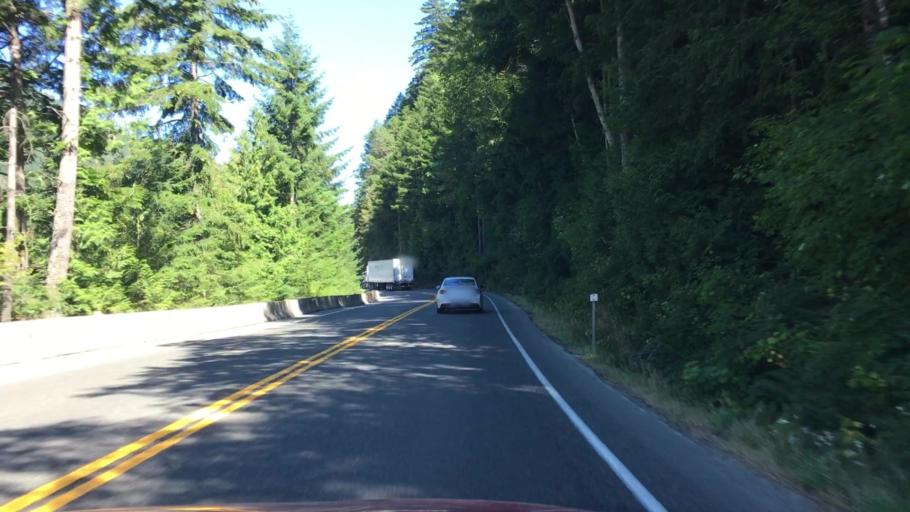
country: CA
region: British Columbia
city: Port Alberni
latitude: 49.2885
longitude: -124.6132
